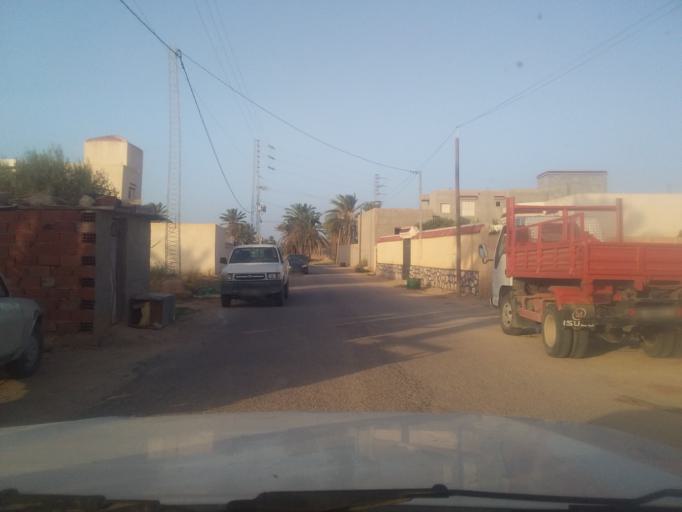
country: TN
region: Qabis
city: Gabes
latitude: 33.6226
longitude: 10.2939
